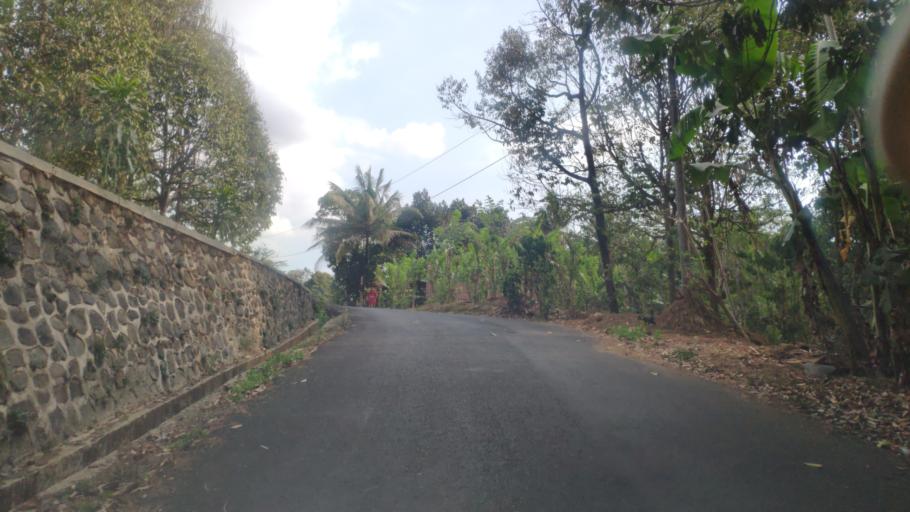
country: ID
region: Central Java
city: Purbalingga
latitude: -7.3747
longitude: 109.5354
